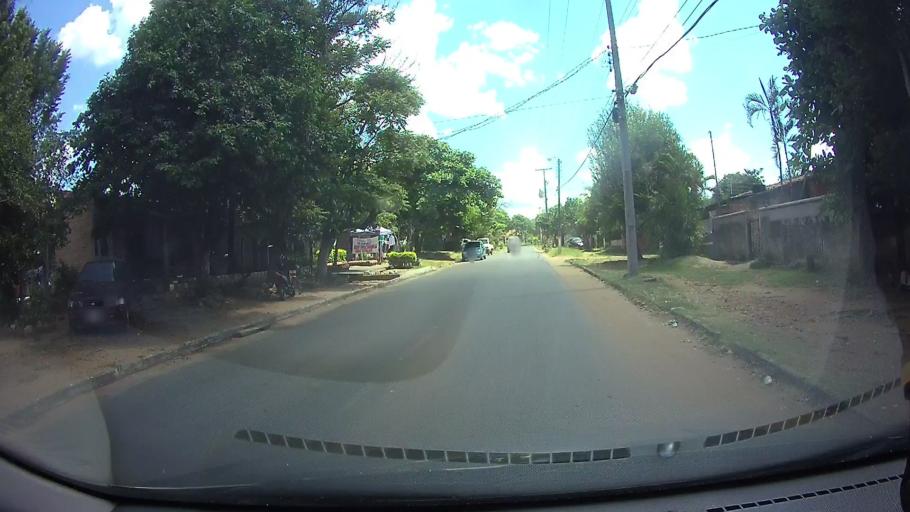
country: PY
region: Central
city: Limpio
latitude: -25.1676
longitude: -57.4380
